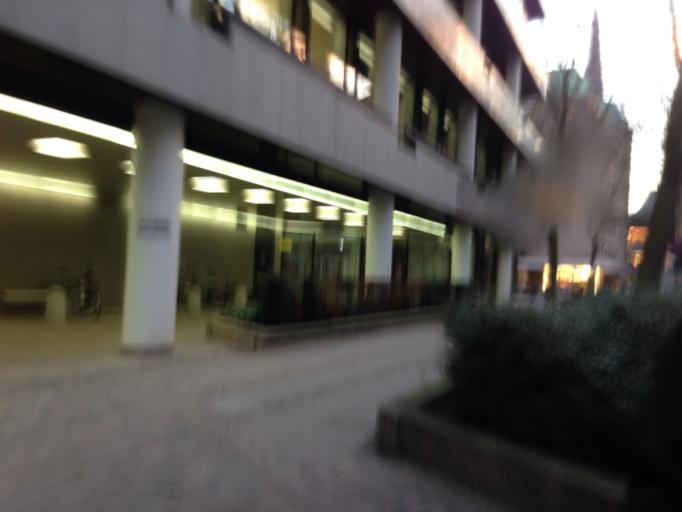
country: DE
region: Hamburg
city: Altstadt
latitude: 53.5522
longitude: 9.9995
